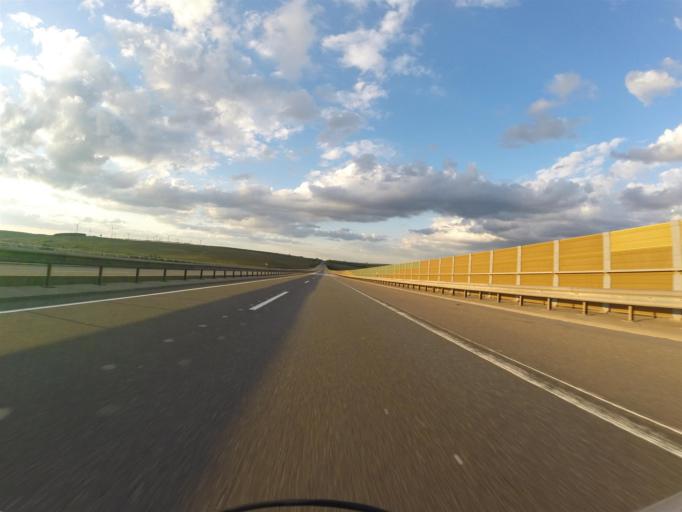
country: DE
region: Rheinland-Pfalz
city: Freimersheim
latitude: 49.7309
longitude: 8.0817
